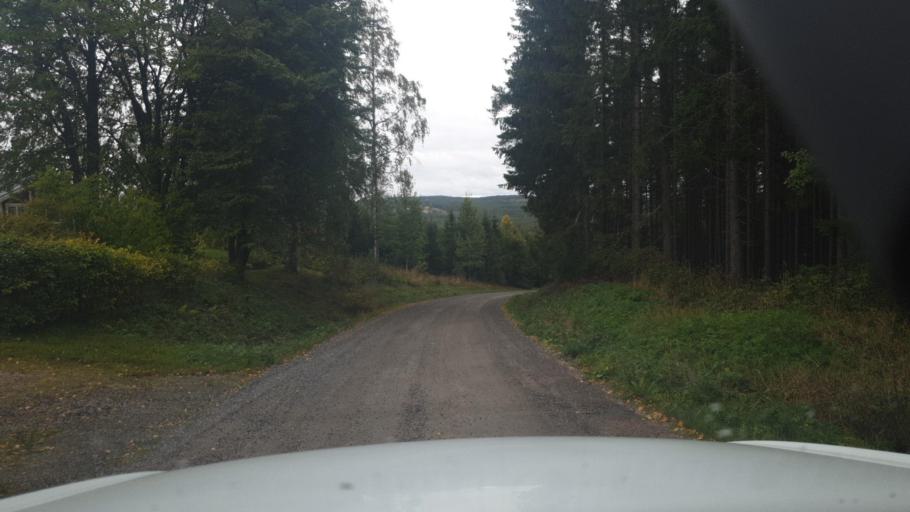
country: SE
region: Vaermland
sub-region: Torsby Kommun
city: Torsby
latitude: 60.1840
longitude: 12.6445
